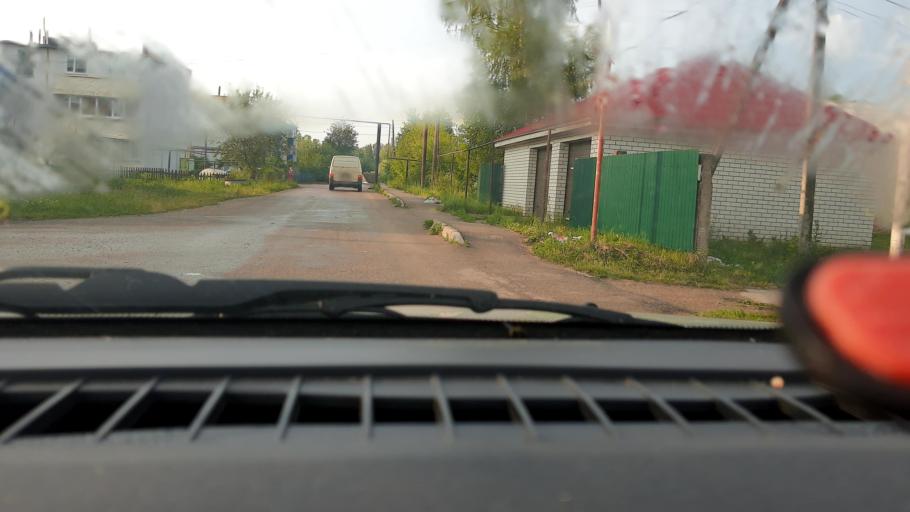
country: RU
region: Nizjnij Novgorod
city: Lukoyanov
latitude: 55.0433
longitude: 44.4942
